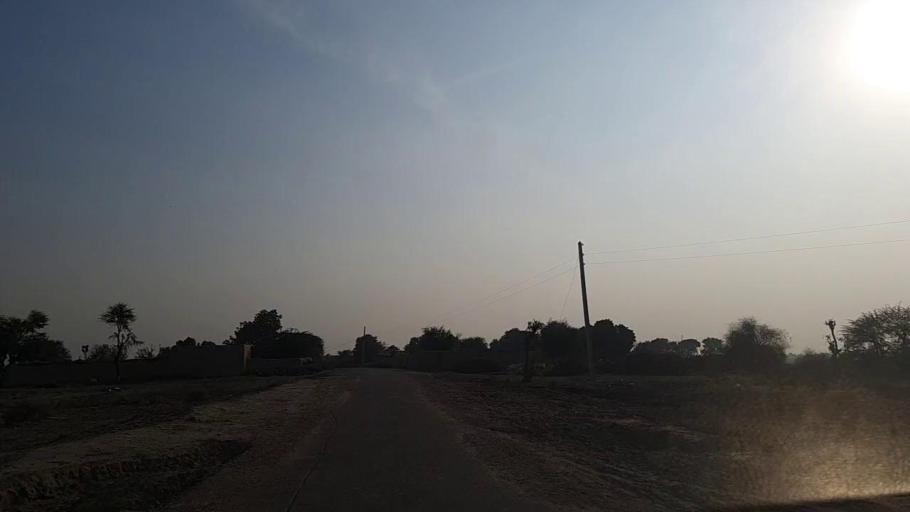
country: PK
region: Sindh
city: Jam Sahib
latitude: 26.4475
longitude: 68.5835
